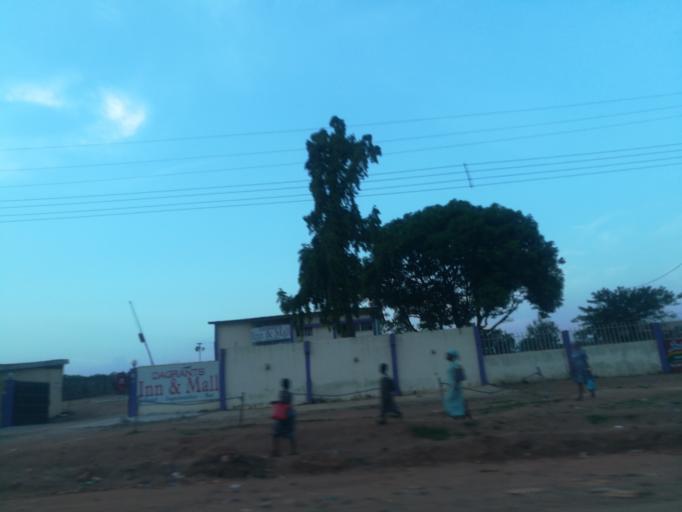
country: NG
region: Ogun
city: Abeokuta
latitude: 7.1775
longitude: 3.3915
